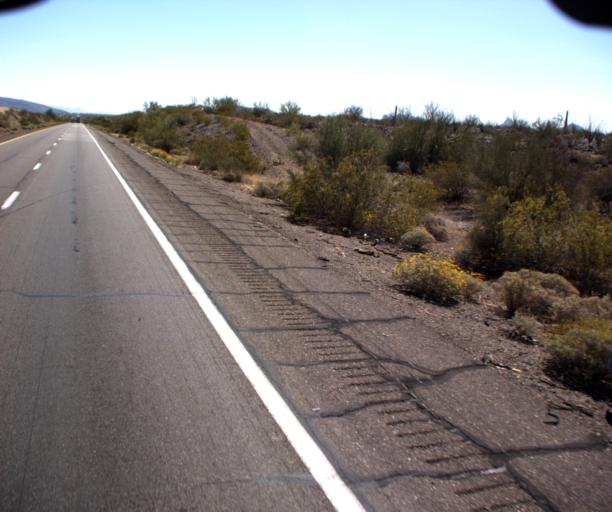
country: US
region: Arizona
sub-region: La Paz County
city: Quartzsite
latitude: 33.6607
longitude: -114.0049
